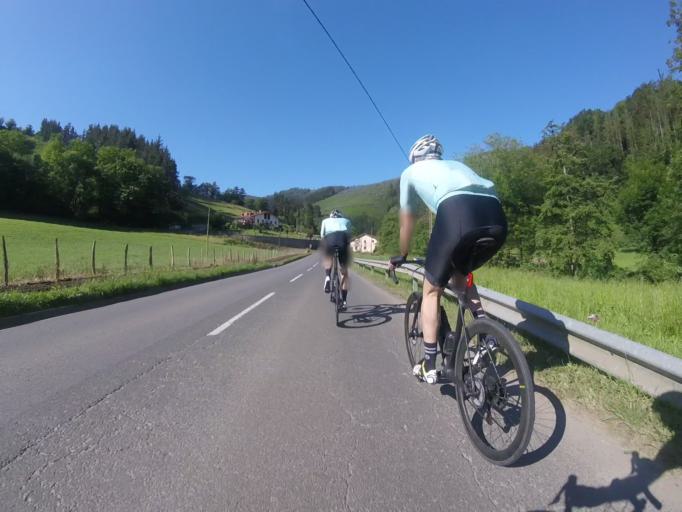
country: ES
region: Basque Country
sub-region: Provincia de Guipuzcoa
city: Beizama
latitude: 43.1434
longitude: -2.2344
